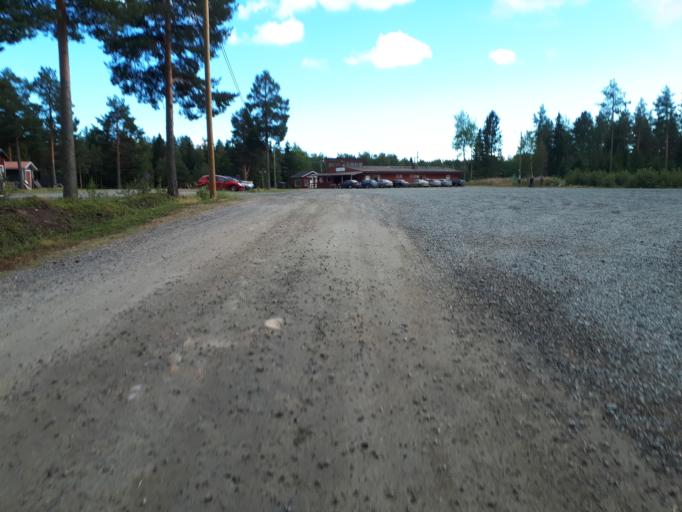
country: FI
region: Northern Ostrobothnia
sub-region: Oulunkaari
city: Ii
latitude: 65.3318
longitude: 25.3897
